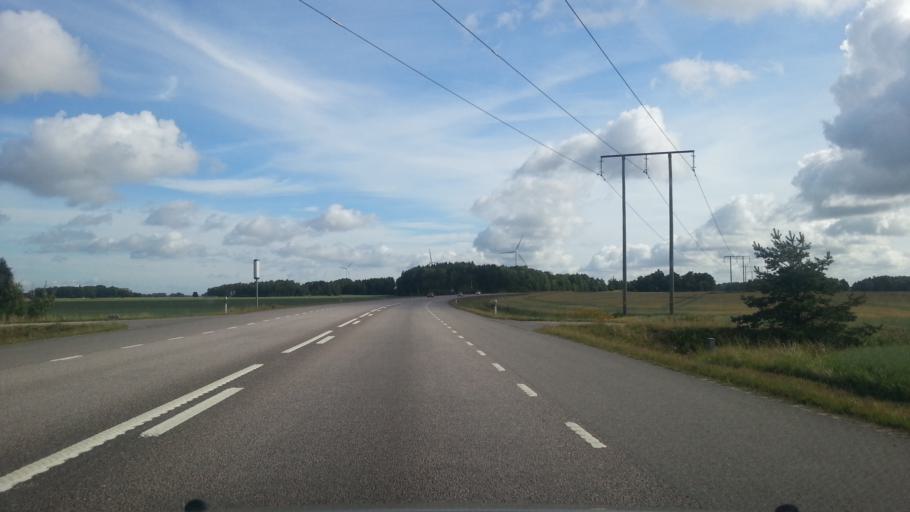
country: SE
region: Vaestra Goetaland
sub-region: Grastorps Kommun
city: Graestorp
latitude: 58.3166
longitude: 12.5643
